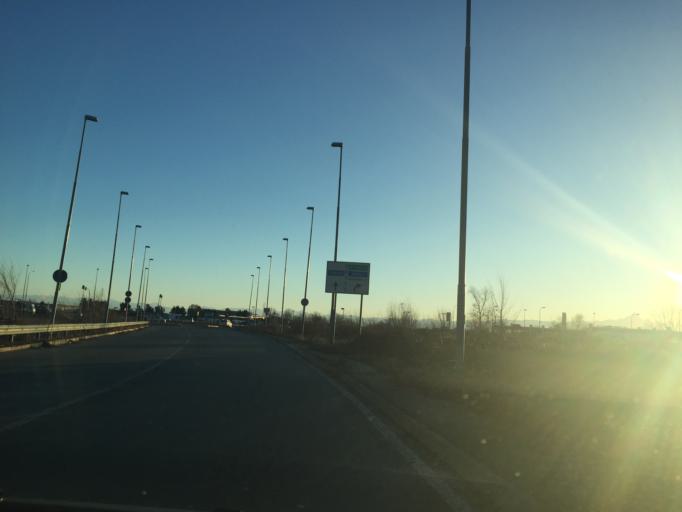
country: IT
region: Piedmont
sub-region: Provincia di Torino
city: Gerbido
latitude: 45.0529
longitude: 7.6048
